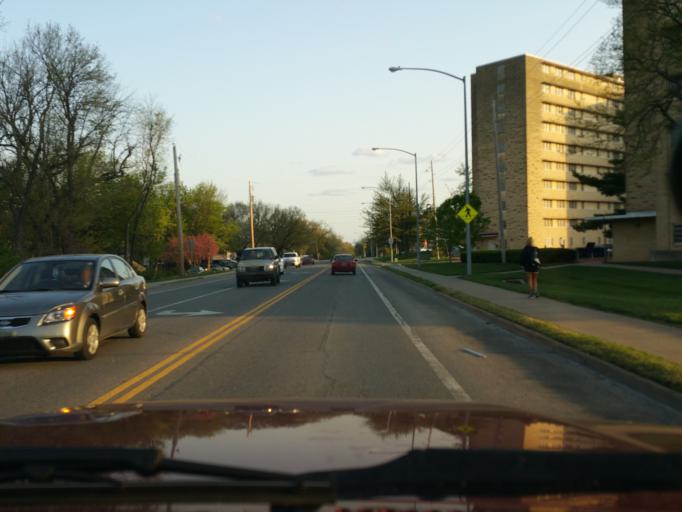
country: US
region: Kansas
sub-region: Riley County
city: Manhattan
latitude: 39.1950
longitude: -96.5764
